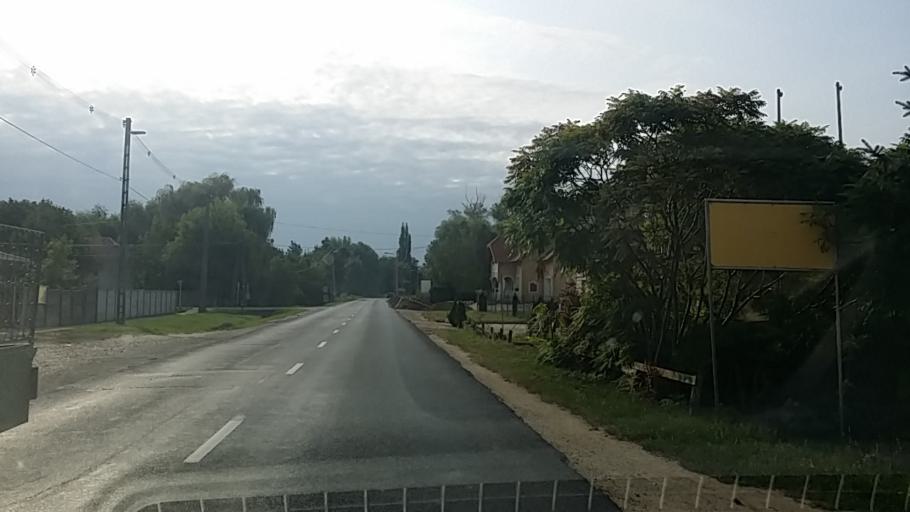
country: HU
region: Gyor-Moson-Sopron
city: Fertoszentmiklos
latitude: 47.6025
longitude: 16.9098
